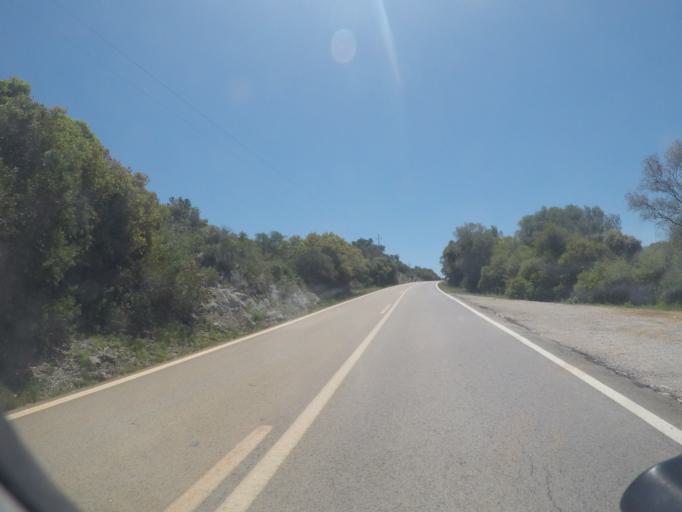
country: PT
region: Setubal
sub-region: Sesimbra
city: Sesimbra
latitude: 38.4663
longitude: -9.0269
